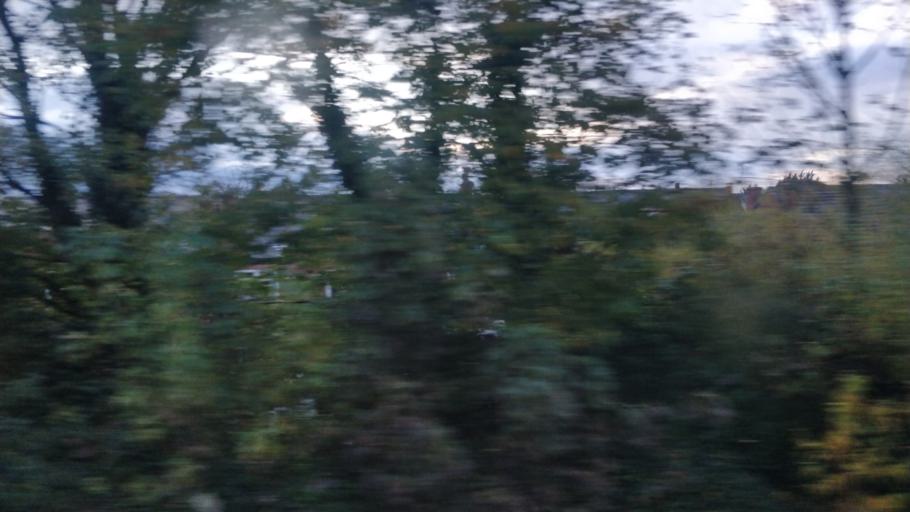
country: GB
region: England
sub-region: Sefton
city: Southport
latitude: 53.6410
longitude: -2.9714
